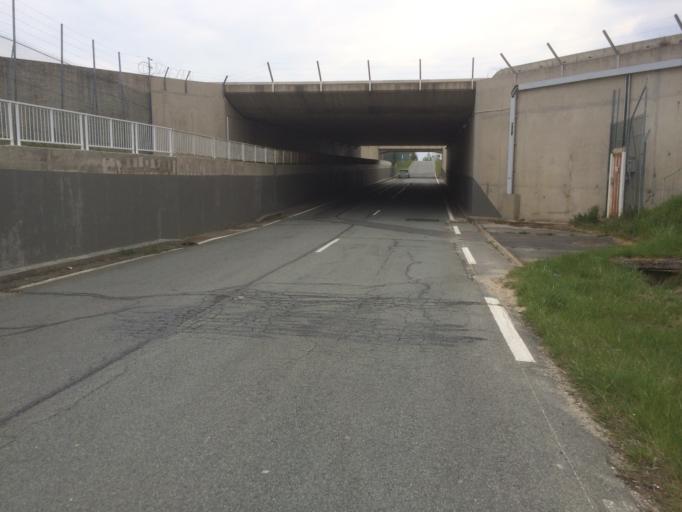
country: FR
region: Ile-de-France
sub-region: Departement de l'Essonne
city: Paray-Vieille-Poste
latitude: 48.7248
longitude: 2.3464
